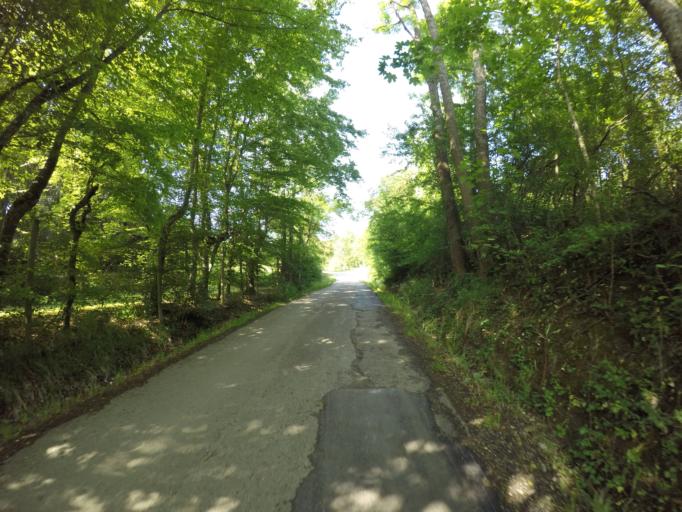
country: DE
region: Baden-Wuerttemberg
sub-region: Tuebingen Region
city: Reutlingen
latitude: 48.4813
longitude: 9.1787
